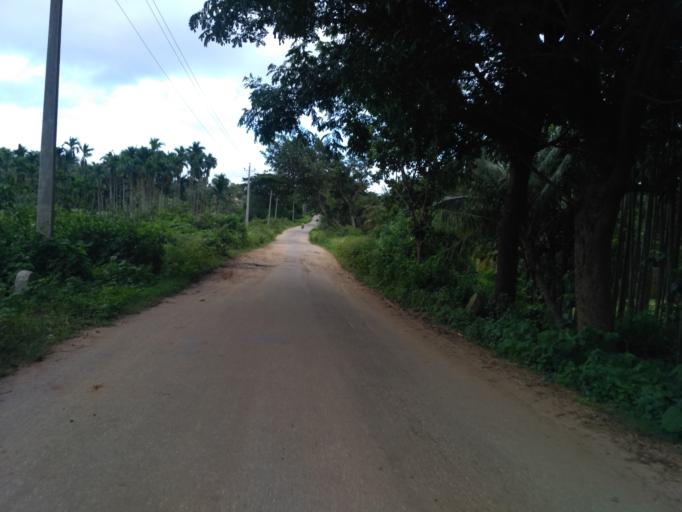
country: IN
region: Karnataka
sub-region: Hassan
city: Gorur
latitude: 12.8315
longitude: 76.0979
